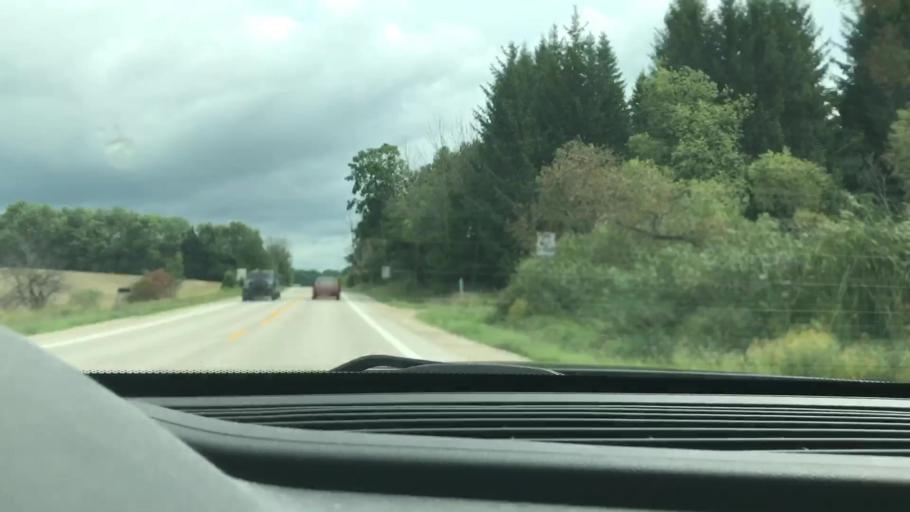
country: US
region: Michigan
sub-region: Antrim County
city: Bellaire
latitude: 45.0954
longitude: -85.2963
